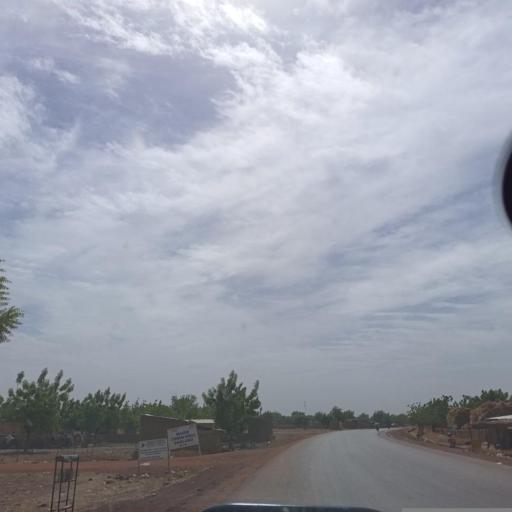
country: ML
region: Koulikoro
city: Kolokani
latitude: 13.2023
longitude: -7.9315
